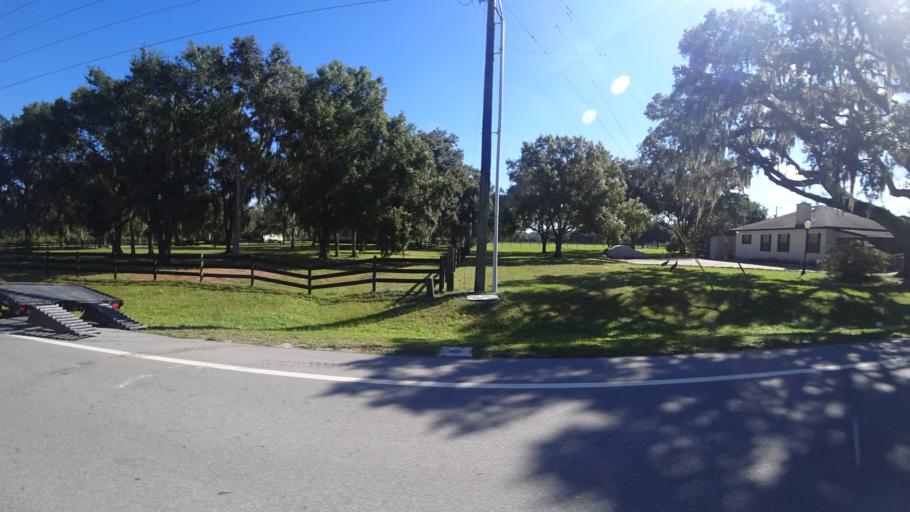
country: US
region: Florida
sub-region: Manatee County
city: Ellenton
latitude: 27.5630
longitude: -82.4254
